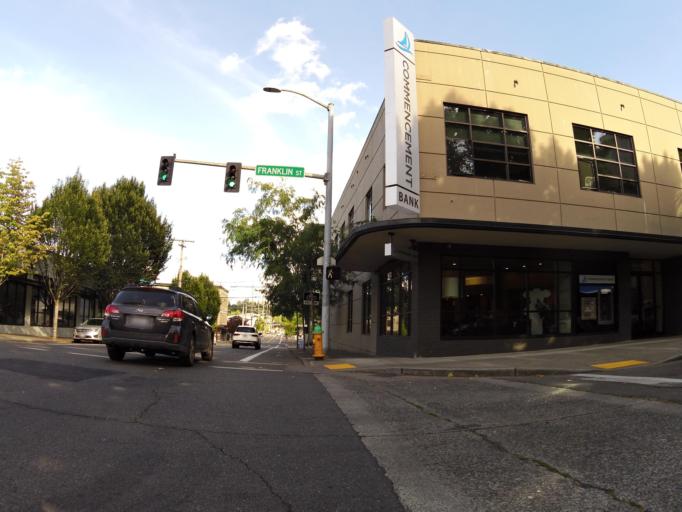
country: US
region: Washington
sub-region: Thurston County
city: Olympia
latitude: 47.0434
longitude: -122.8990
